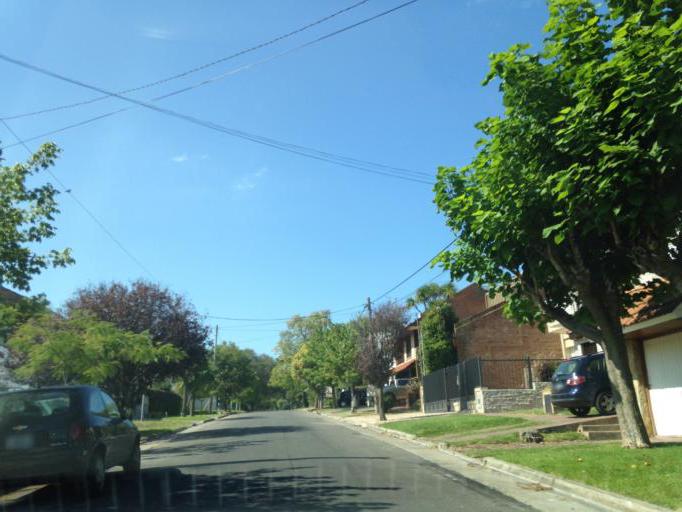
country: AR
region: Buenos Aires
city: Mar del Plata
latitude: -38.0309
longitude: -57.5469
